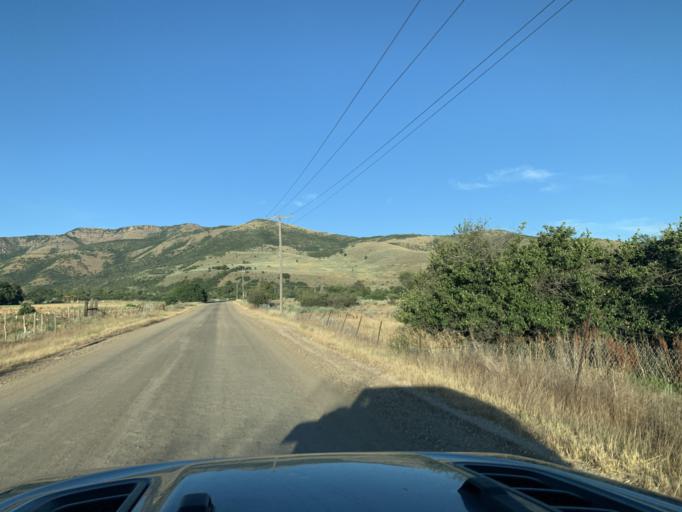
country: US
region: Utah
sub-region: Weber County
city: Wolf Creek
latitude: 41.2931
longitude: -111.7606
